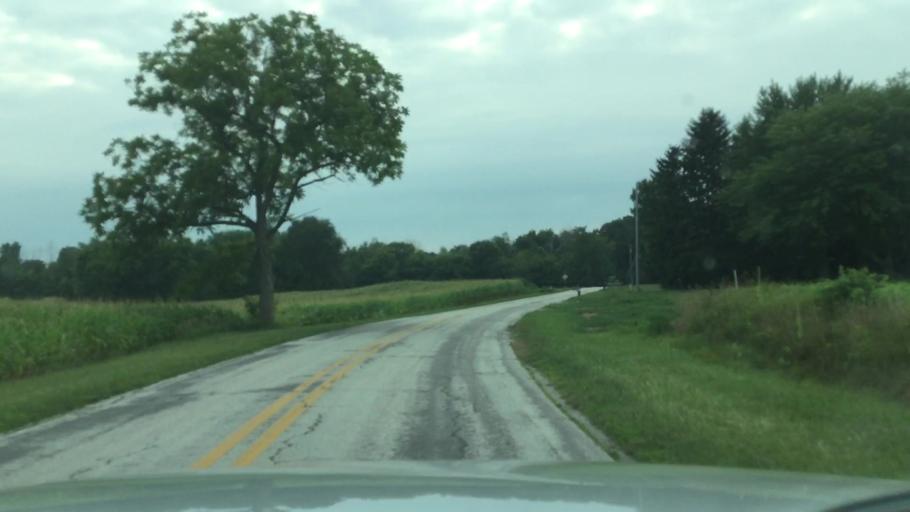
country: US
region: Michigan
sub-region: Saginaw County
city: Frankenmuth
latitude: 43.3321
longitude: -83.7933
